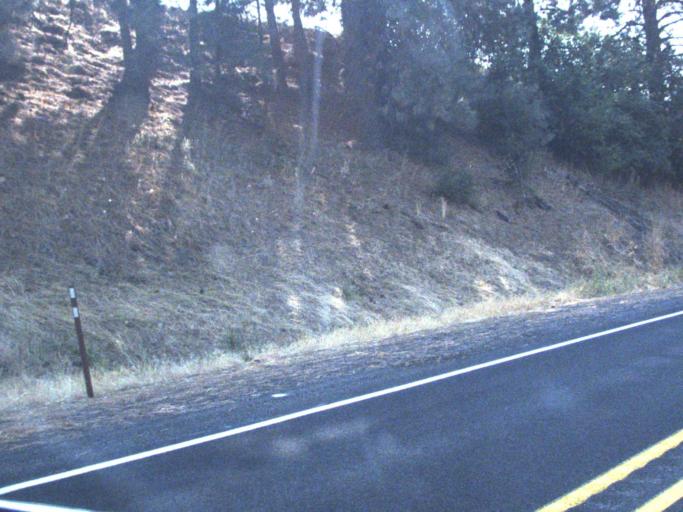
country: US
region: Washington
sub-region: Whitman County
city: Pullman
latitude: 46.9651
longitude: -117.1091
